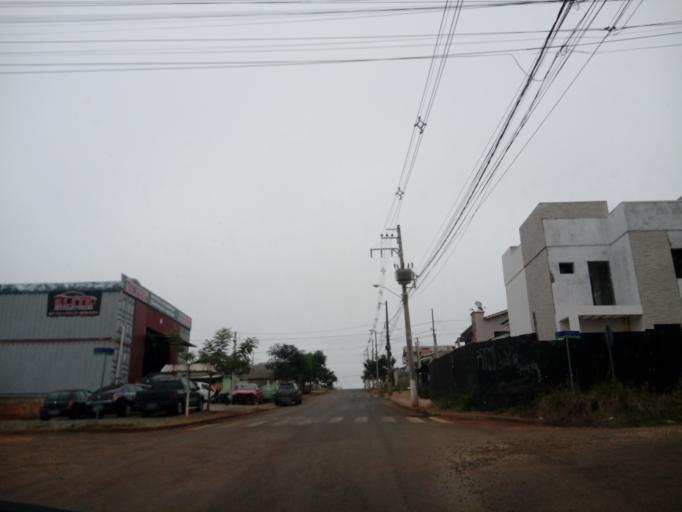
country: BR
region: Santa Catarina
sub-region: Chapeco
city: Chapeco
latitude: -27.1066
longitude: -52.6706
